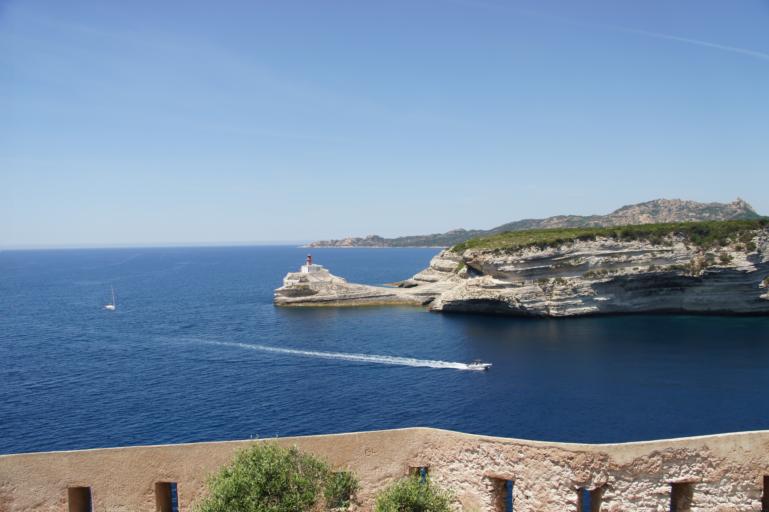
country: FR
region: Corsica
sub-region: Departement de la Corse-du-Sud
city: Bonifacio
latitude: 41.3861
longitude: 9.1490
